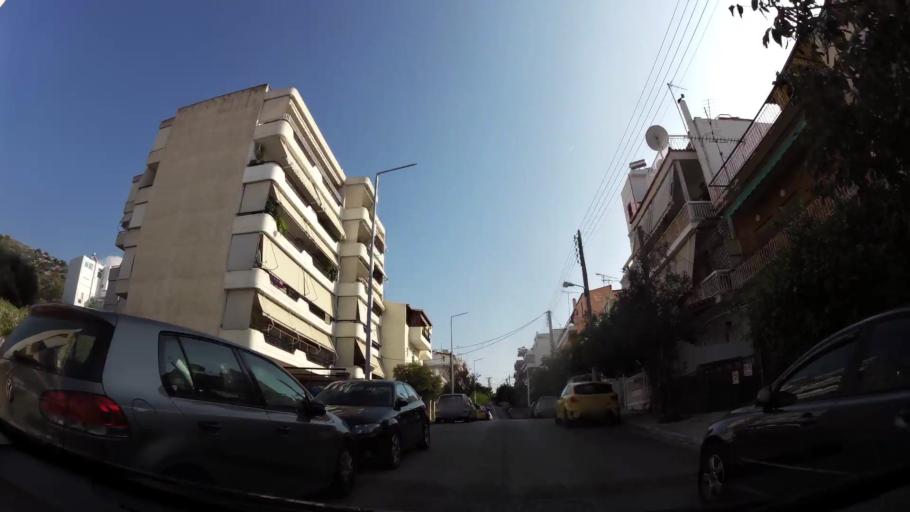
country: GR
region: Attica
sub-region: Nomarchia Athinas
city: Argyroupoli
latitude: 37.9010
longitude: 23.7570
